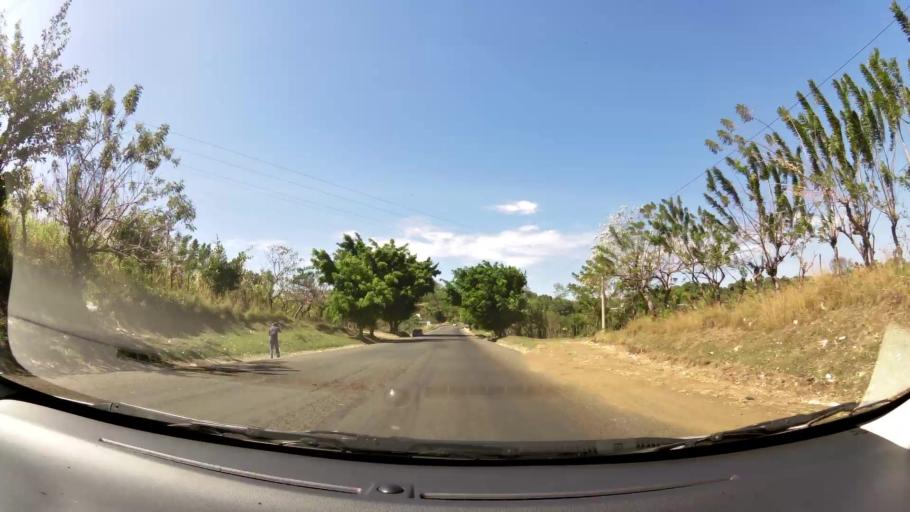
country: SV
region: Ahuachapan
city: Ahuachapan
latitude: 13.9367
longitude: -89.8526
